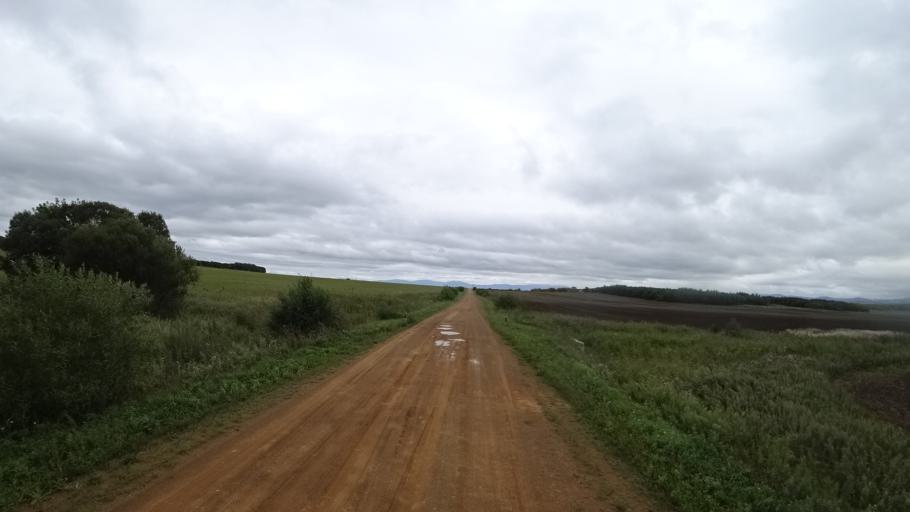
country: RU
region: Primorskiy
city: Chernigovka
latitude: 44.4364
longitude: 132.5851
